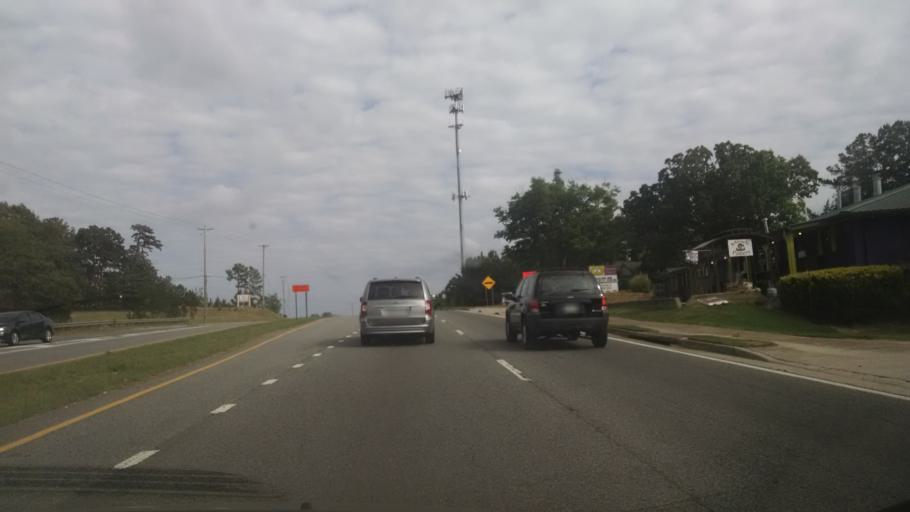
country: US
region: Georgia
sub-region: Forsyth County
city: Cumming
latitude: 34.1667
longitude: -84.1216
